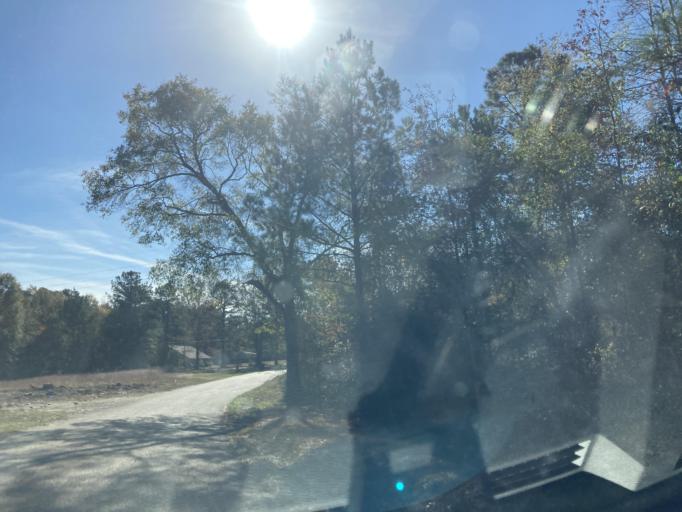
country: US
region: Mississippi
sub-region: Lamar County
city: Sumrall
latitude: 31.2654
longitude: -89.5284
